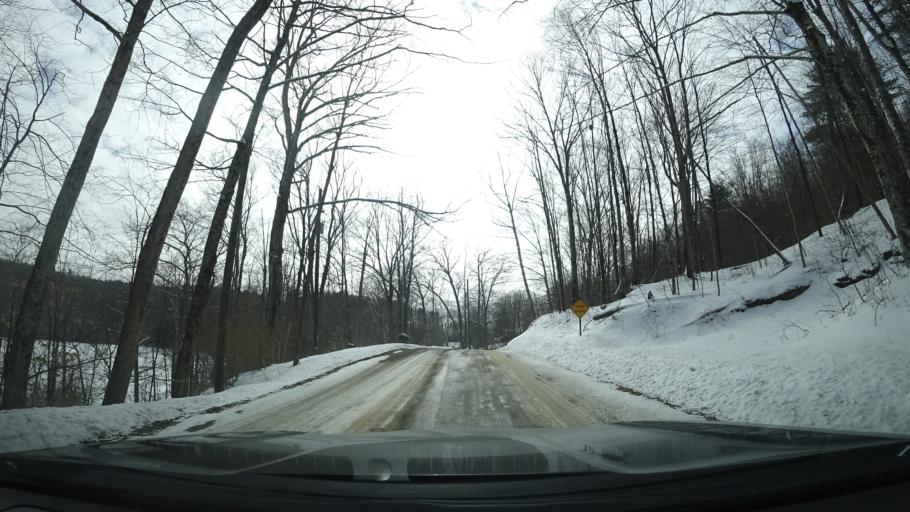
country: US
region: New York
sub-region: Washington County
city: Cambridge
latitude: 43.2139
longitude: -73.3576
